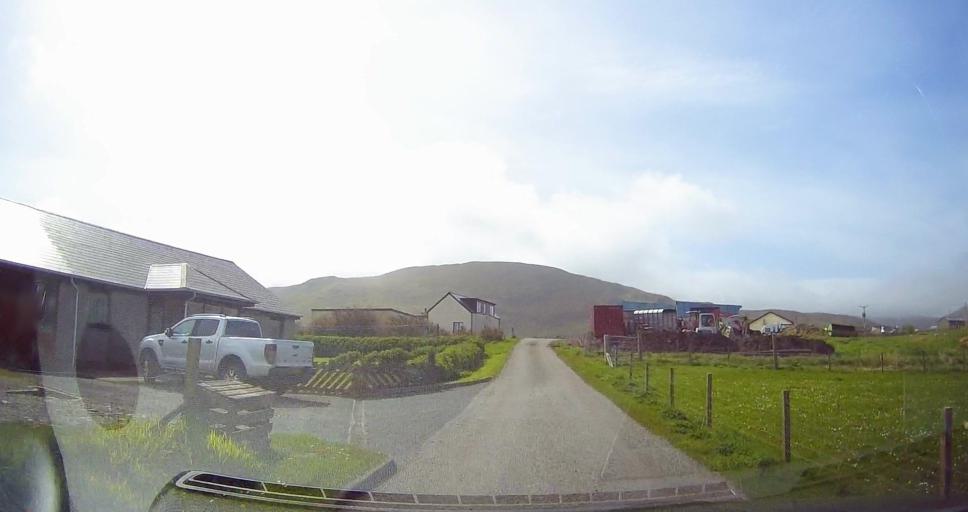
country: GB
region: Scotland
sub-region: Shetland Islands
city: Sandwick
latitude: 60.0392
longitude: -1.2244
